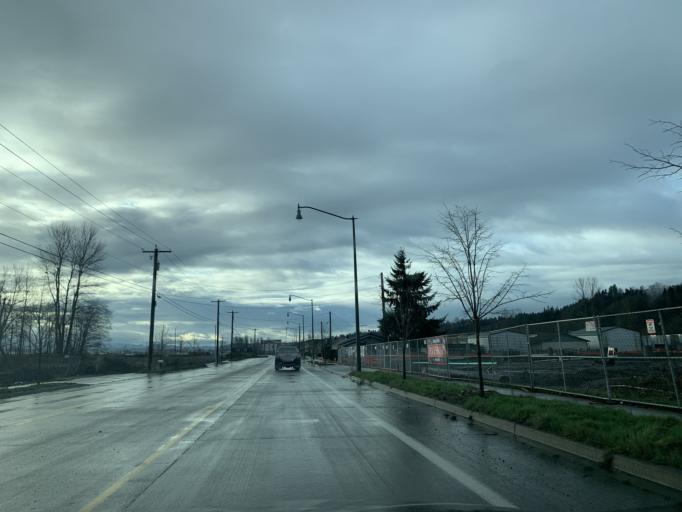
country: US
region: Washington
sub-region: King County
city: Pacific
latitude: 47.2394
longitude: -122.2488
